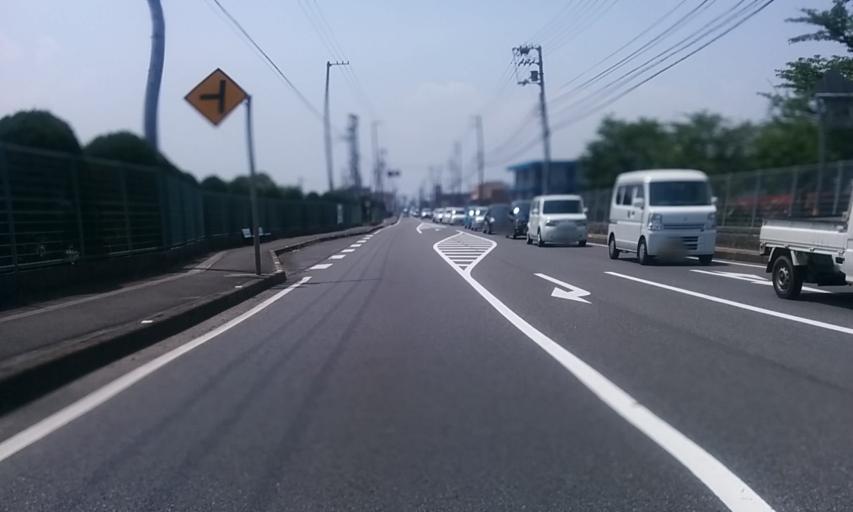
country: JP
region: Ehime
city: Saijo
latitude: 33.9132
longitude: 133.2077
